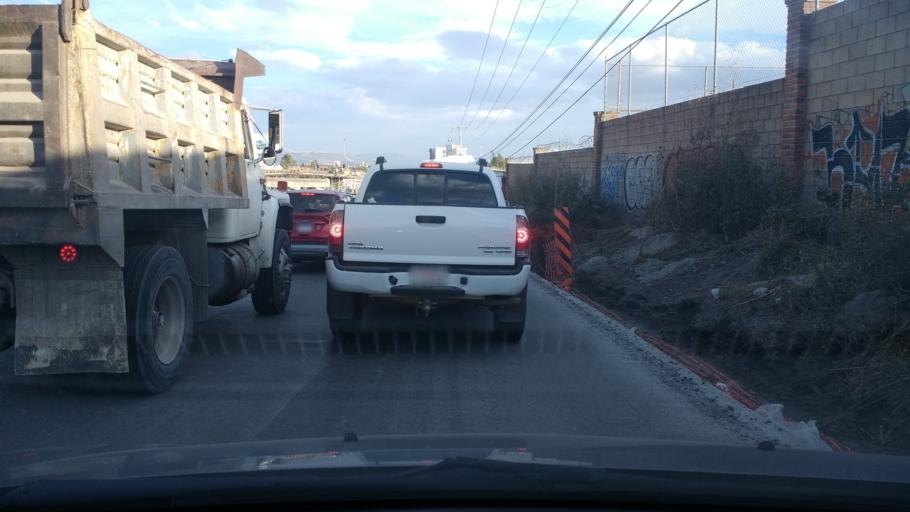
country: MX
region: Guanajuato
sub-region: Leon
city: La Ermita
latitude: 21.1707
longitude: -101.6997
